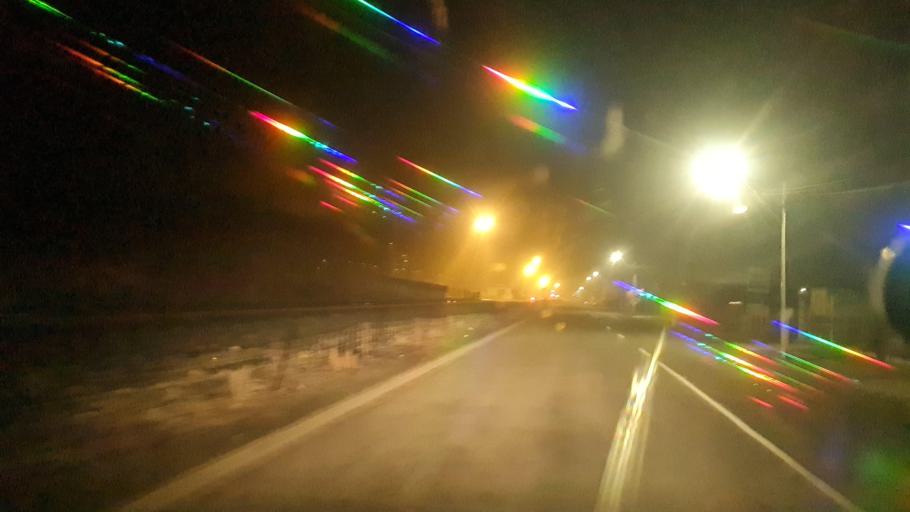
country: NZ
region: Otago
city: Oamaru
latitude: -45.0889
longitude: 170.9813
